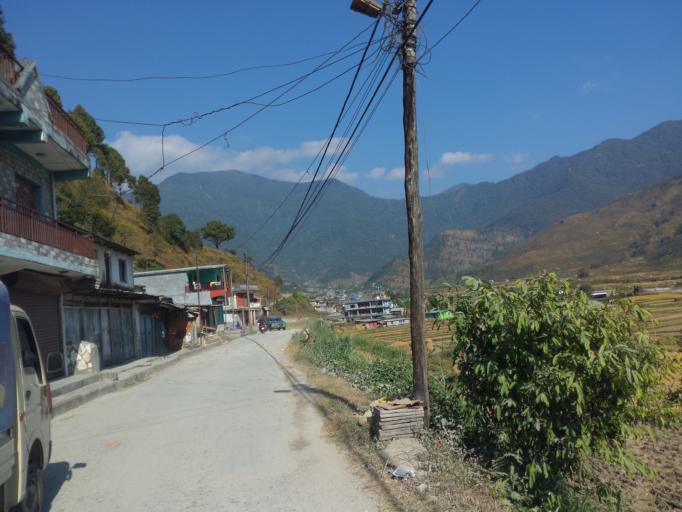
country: NP
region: Western Region
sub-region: Gandaki Zone
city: Pokhara
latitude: 28.2736
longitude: 83.9807
